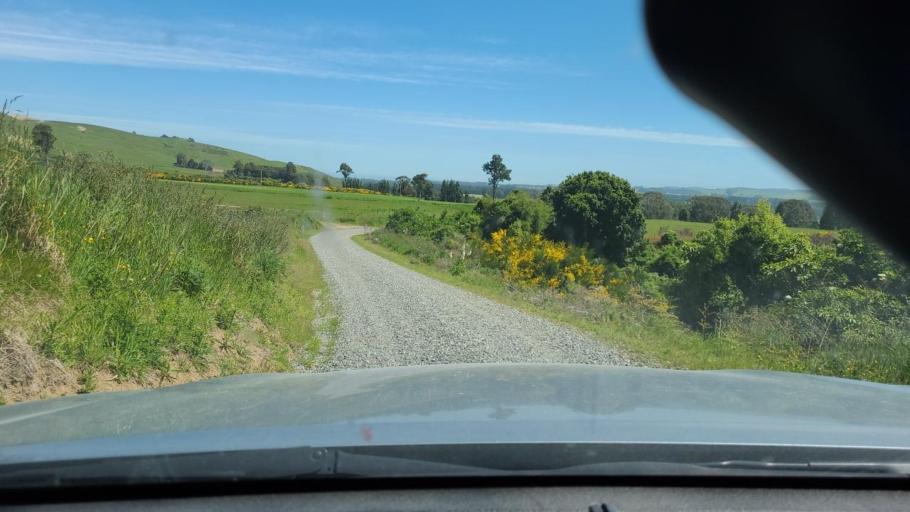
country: NZ
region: Southland
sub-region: Southland District
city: Riverton
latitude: -46.0480
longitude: 167.7590
